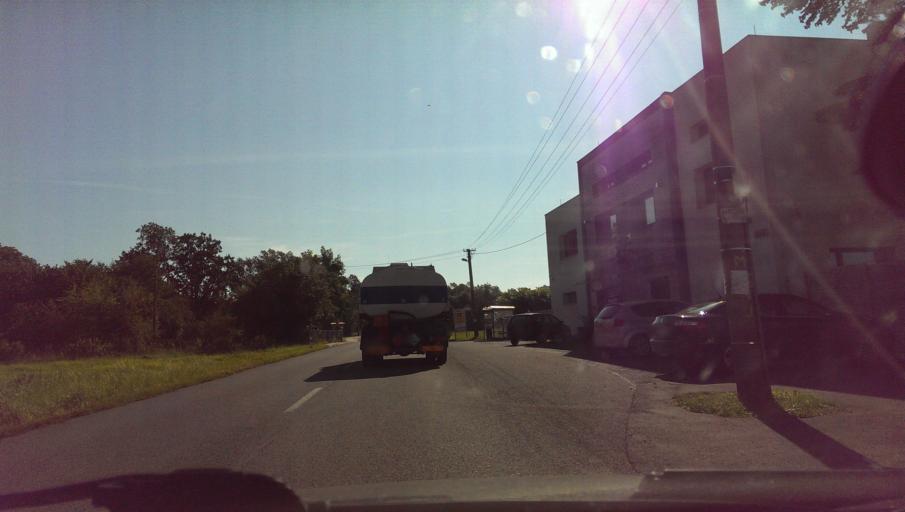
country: CZ
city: Frycovice
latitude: 49.6838
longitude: 18.2427
